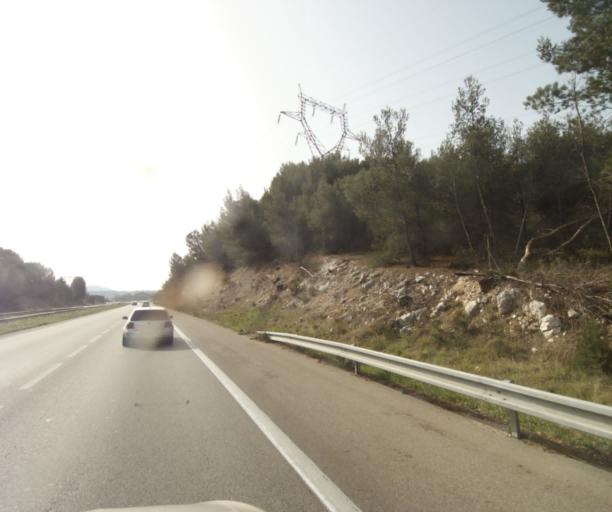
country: FR
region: Provence-Alpes-Cote d'Azur
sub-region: Departement des Bouches-du-Rhone
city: Cabries
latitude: 43.4466
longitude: 5.3957
